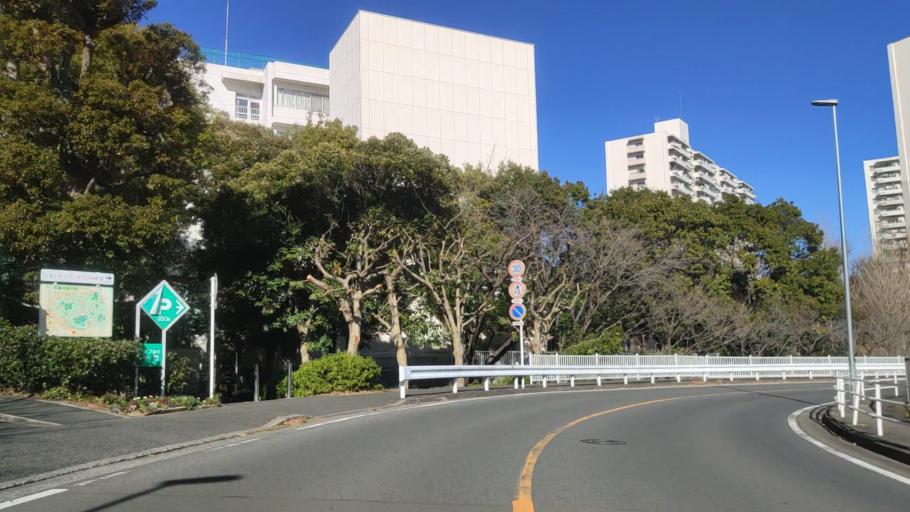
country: JP
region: Kanagawa
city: Minami-rinkan
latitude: 35.5065
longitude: 139.4975
